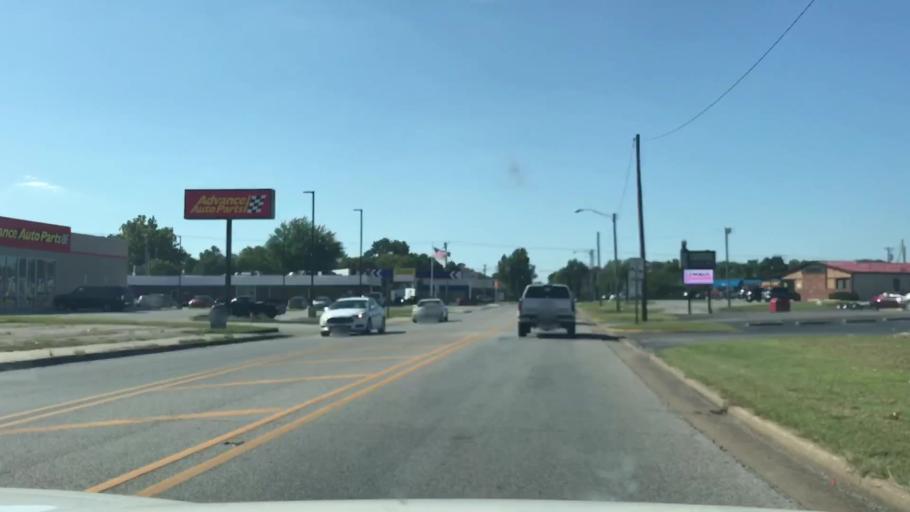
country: US
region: Illinois
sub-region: Madison County
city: Roxana
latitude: 38.8643
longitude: -90.0803
